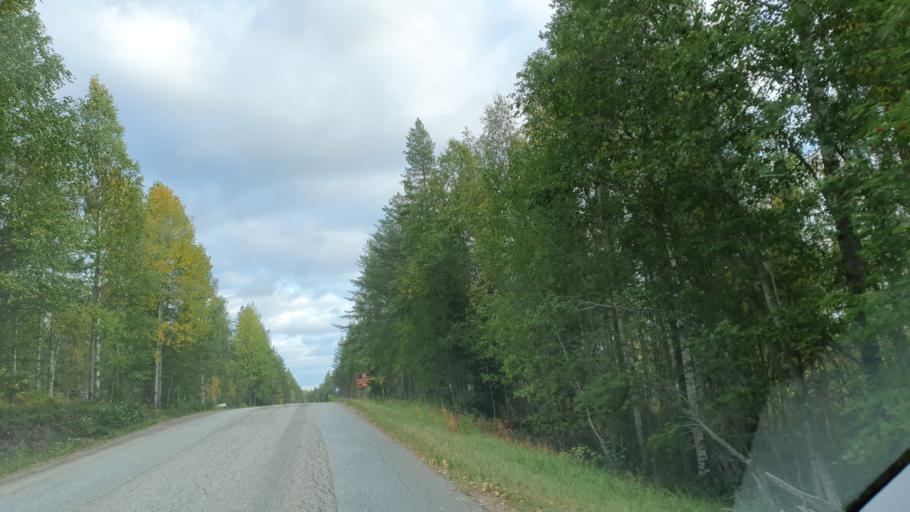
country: FI
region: North Karelia
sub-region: Pielisen Karjala
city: Lieksa
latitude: 63.9130
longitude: 30.1909
